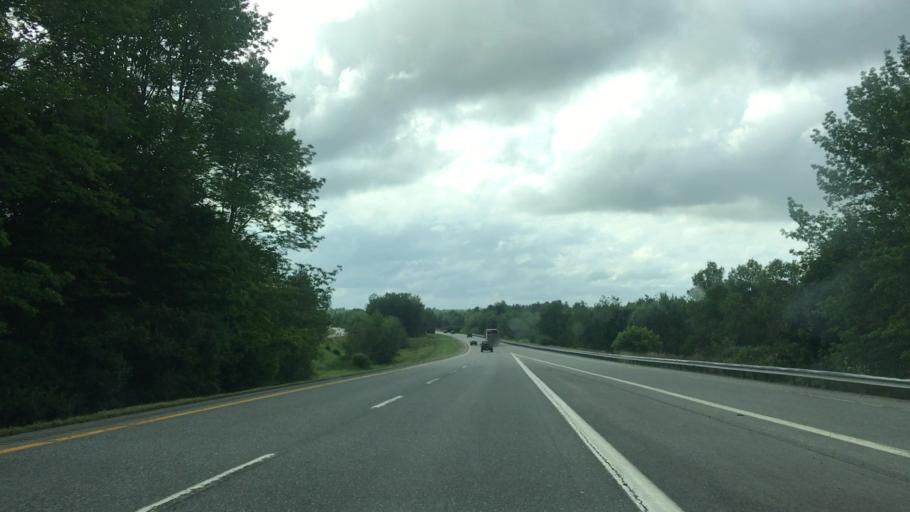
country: US
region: Maine
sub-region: Penobscot County
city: Plymouth
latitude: 44.8056
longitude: -69.2252
